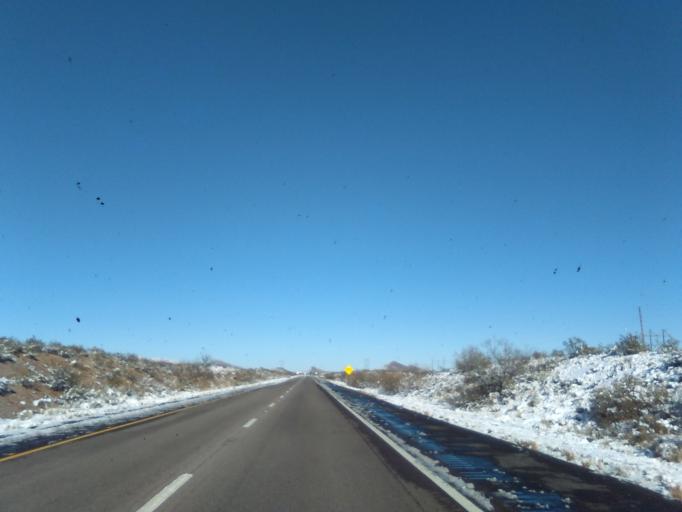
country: US
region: New Mexico
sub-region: Socorro County
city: Socorro
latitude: 33.7104
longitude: -107.0392
